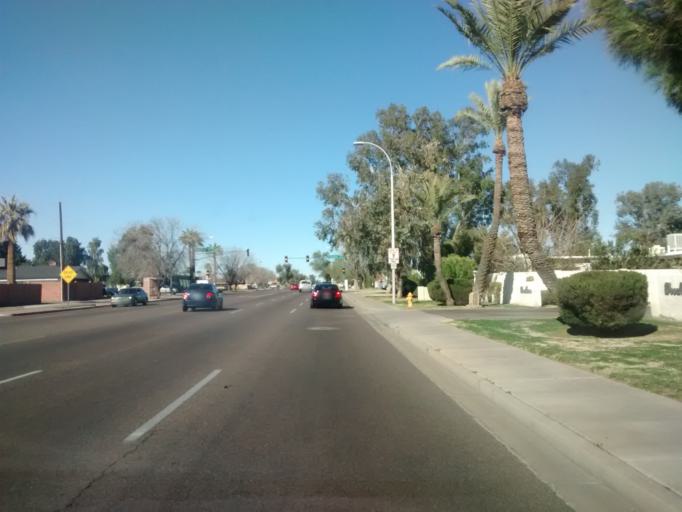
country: US
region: Arizona
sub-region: Maricopa County
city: Glendale
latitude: 33.5302
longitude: -112.1342
